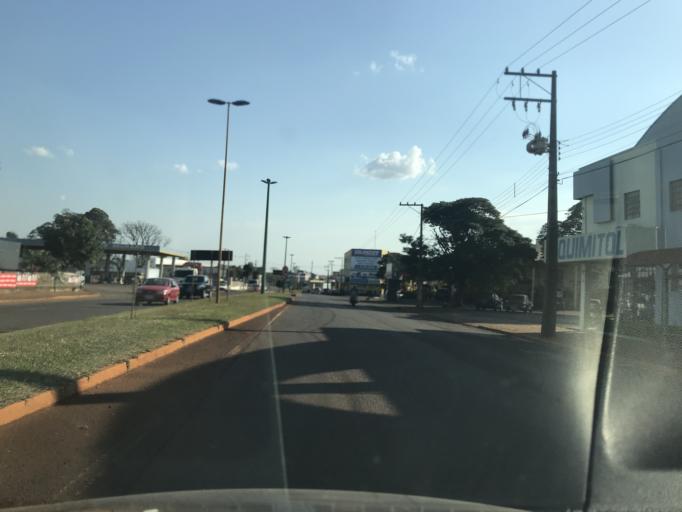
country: BR
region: Parana
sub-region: Toledo
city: Toledo
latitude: -24.7188
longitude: -53.7131
